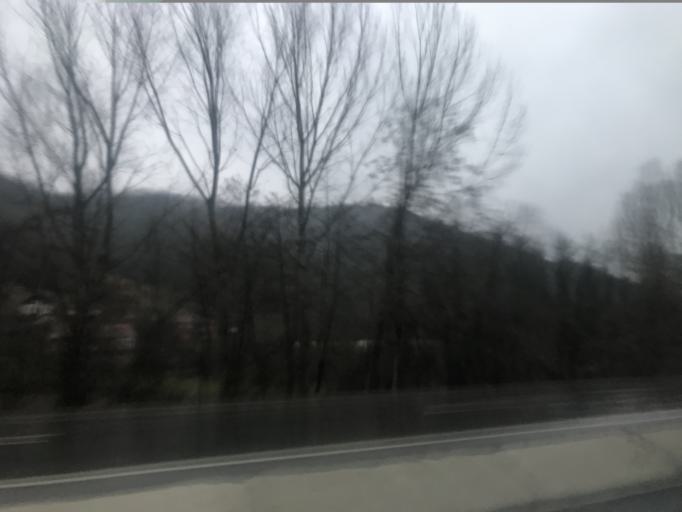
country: TR
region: Zonguldak
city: Gokcebey
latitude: 41.3252
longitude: 32.0564
